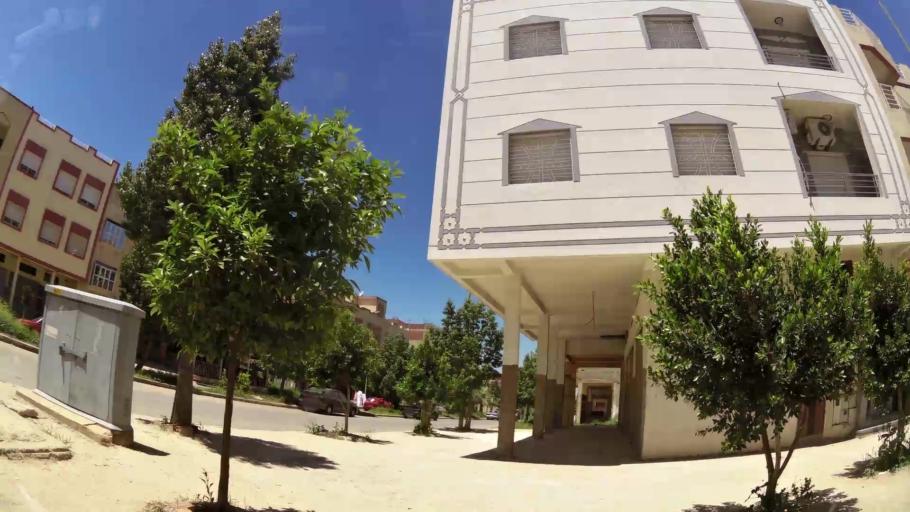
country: MA
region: Meknes-Tafilalet
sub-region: Meknes
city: Meknes
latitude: 33.8516
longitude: -5.5581
